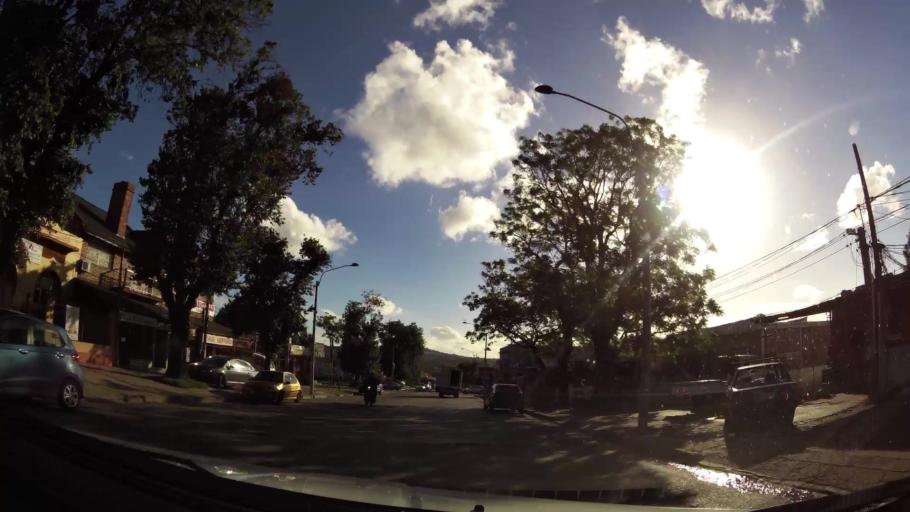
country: UY
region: Montevideo
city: Montevideo
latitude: -34.8685
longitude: -56.2391
